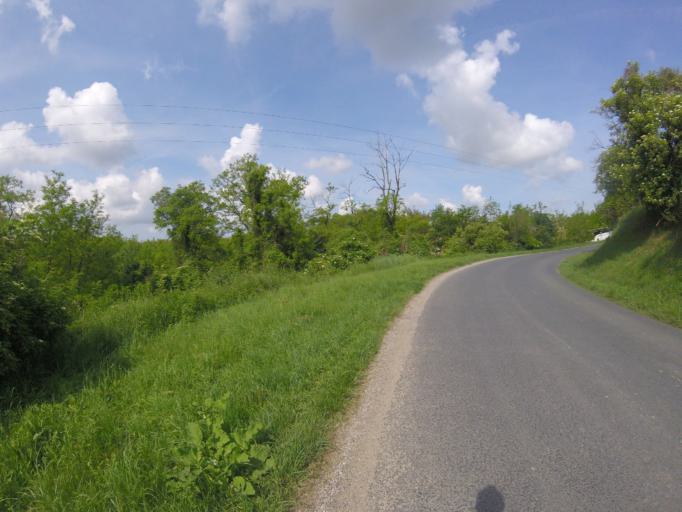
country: HU
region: Veszprem
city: Urkut
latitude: 47.1334
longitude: 17.6287
